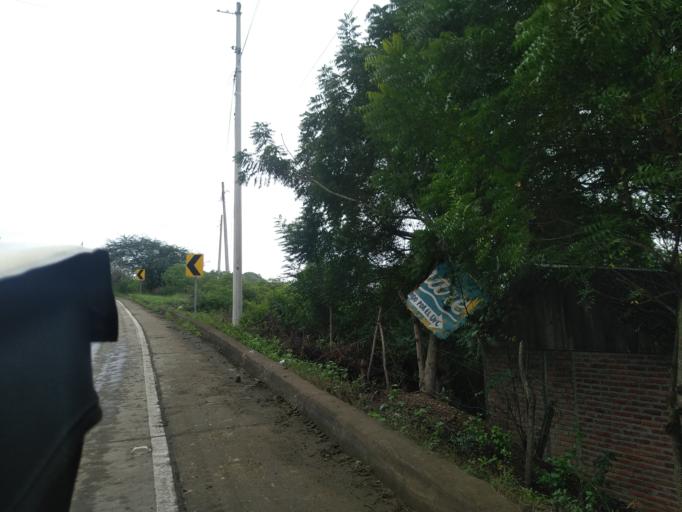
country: EC
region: Manabi
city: Pajan
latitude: -1.6804
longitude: -80.8102
